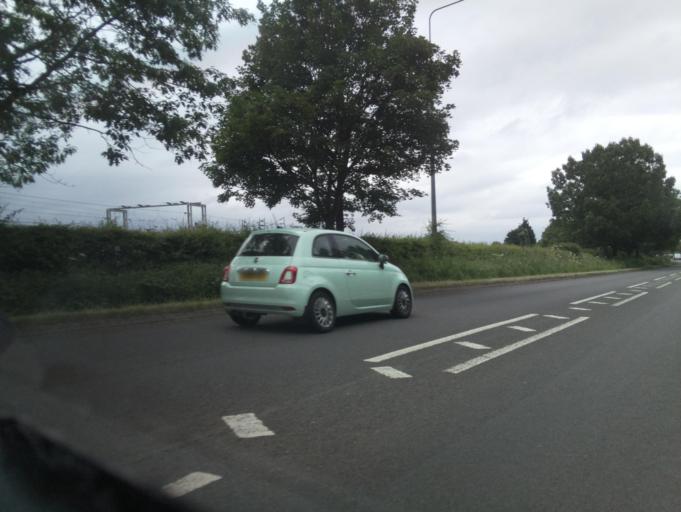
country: GB
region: England
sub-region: Staffordshire
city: Penkridge
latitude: 52.7085
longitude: -2.1245
